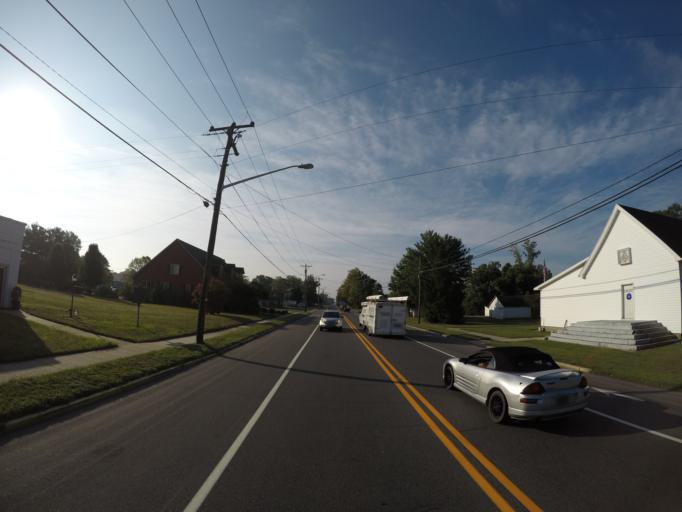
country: US
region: Delaware
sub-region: Sussex County
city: Millsboro
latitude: 38.5515
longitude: -75.2473
